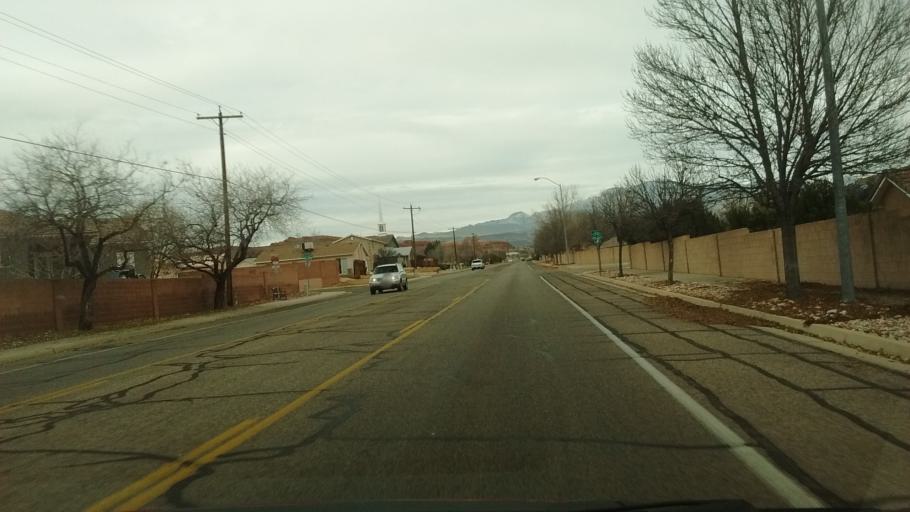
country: US
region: Utah
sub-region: Washington County
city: Washington
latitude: 37.1156
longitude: -113.5317
